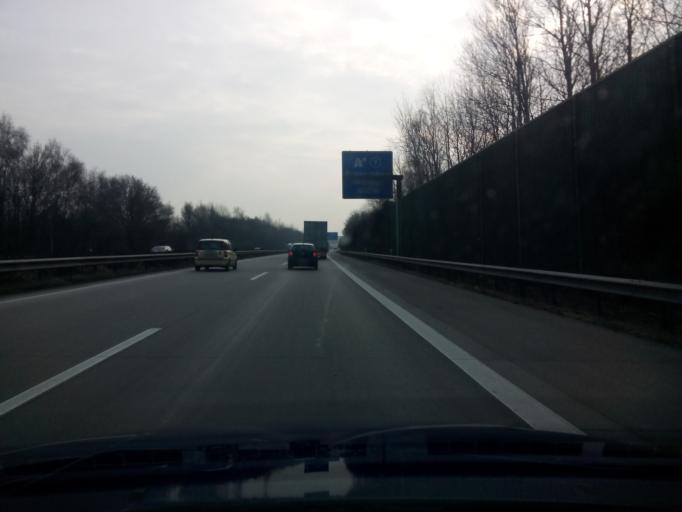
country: DE
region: Lower Saxony
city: Schiffdorf
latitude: 53.5074
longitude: 8.6288
